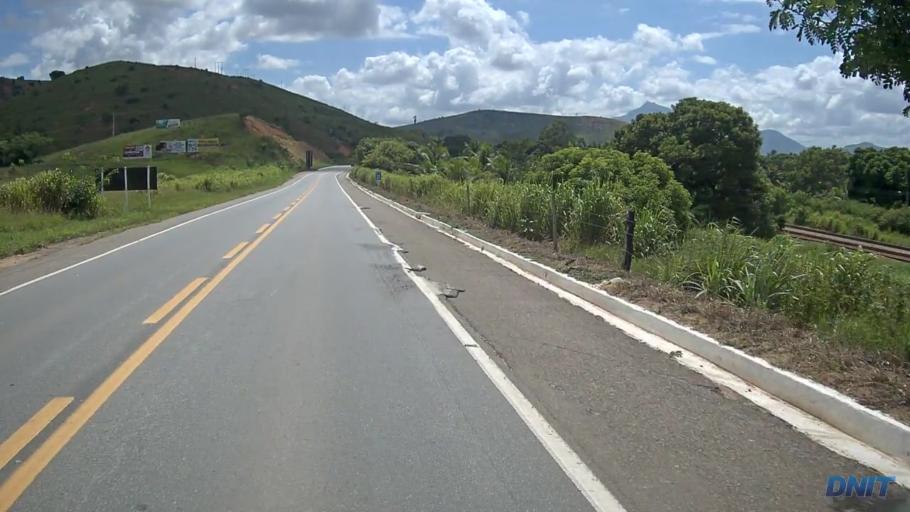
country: BR
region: Minas Gerais
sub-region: Governador Valadares
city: Governador Valadares
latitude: -18.9312
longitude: -42.0462
